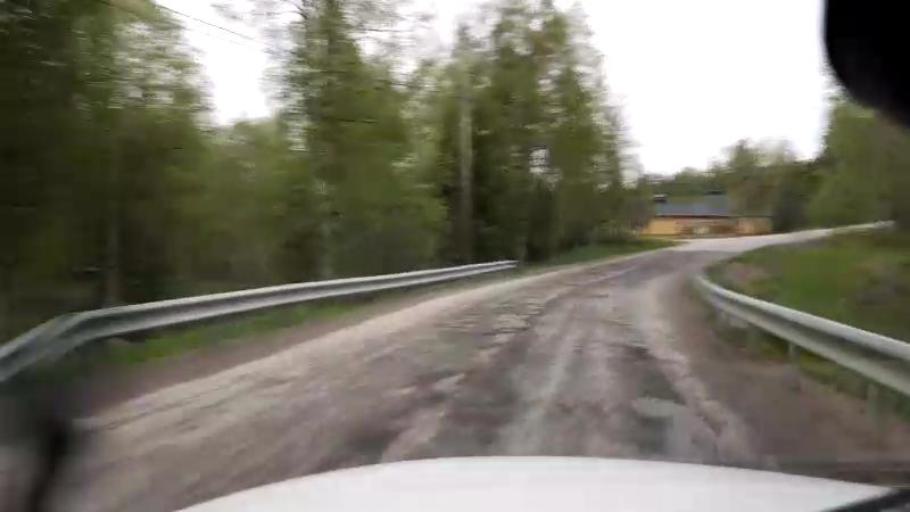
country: SE
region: Gaevleborg
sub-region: Ljusdals Kommun
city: Jaervsoe
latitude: 61.7894
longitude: 16.2174
